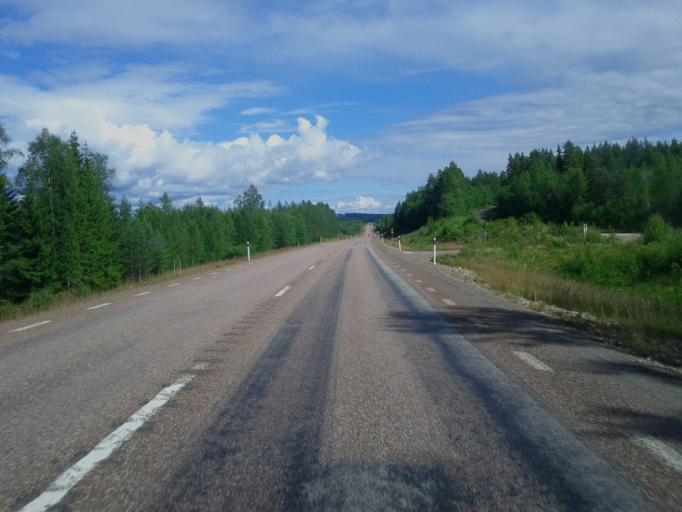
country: SE
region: Dalarna
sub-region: Rattviks Kommun
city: Raettvik
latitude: 60.8438
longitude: 15.1869
